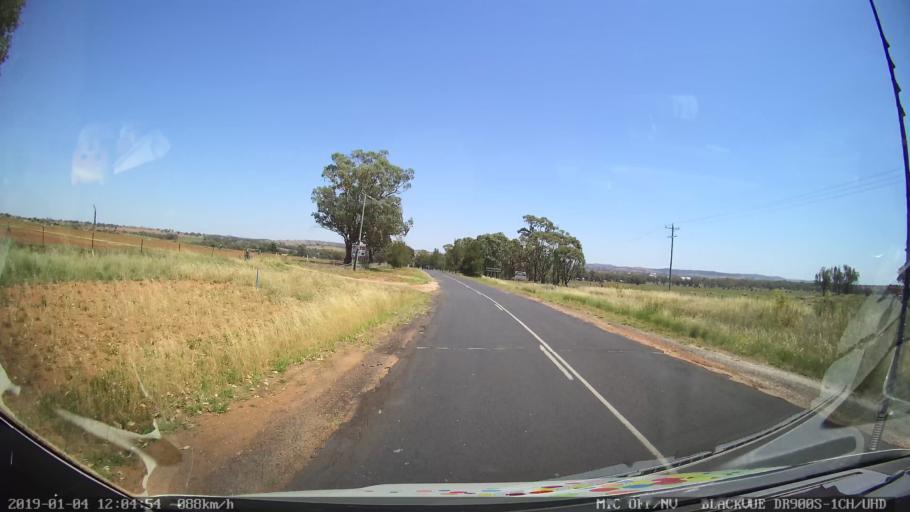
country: AU
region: New South Wales
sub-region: Wellington
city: Wellington
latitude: -32.7591
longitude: 148.6558
